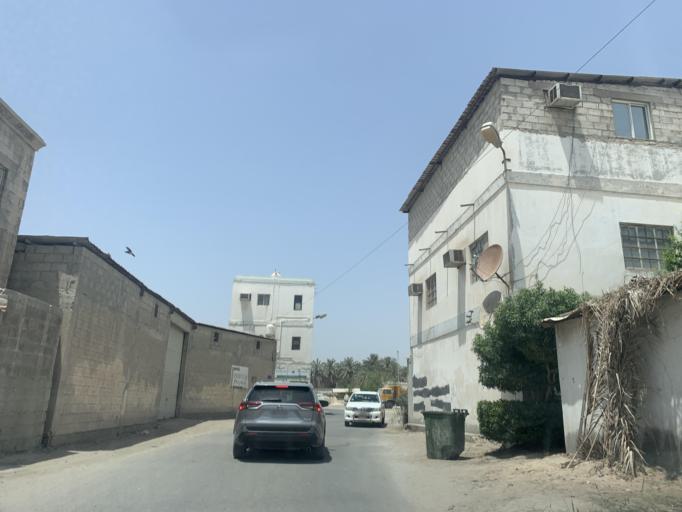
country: BH
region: Central Governorate
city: Madinat Hamad
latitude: 26.1517
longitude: 50.4986
